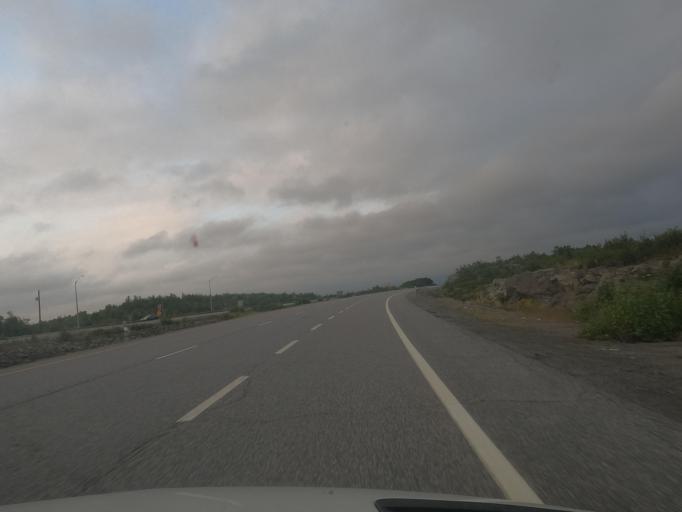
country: CA
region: Ontario
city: Greater Sudbury
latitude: 46.4370
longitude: -80.9656
